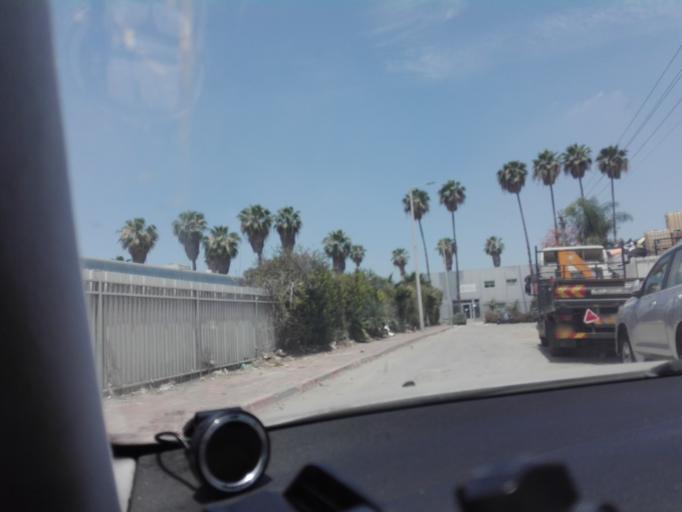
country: IL
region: Central District
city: Bene 'Ayish
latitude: 31.7360
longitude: 34.7568
